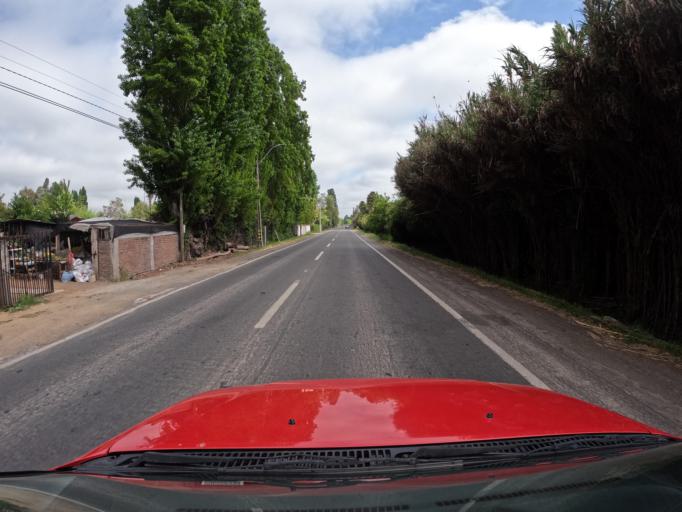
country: CL
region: O'Higgins
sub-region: Provincia de Colchagua
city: Santa Cruz
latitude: -34.6785
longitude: -71.3437
